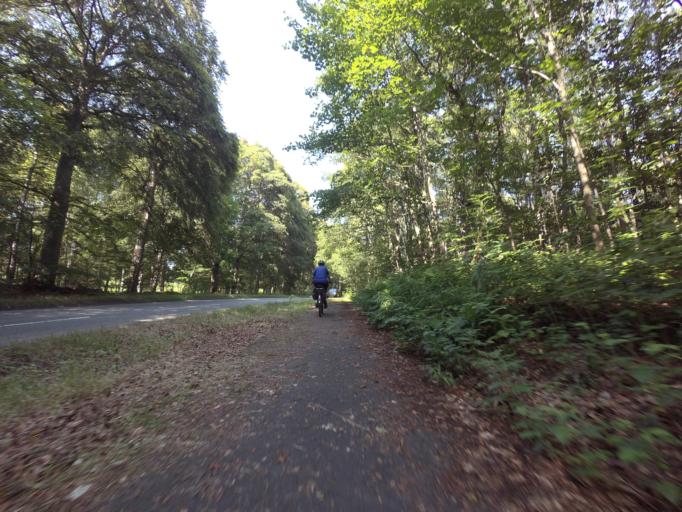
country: GB
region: Scotland
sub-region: Highland
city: Evanton
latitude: 57.6736
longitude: -4.3191
